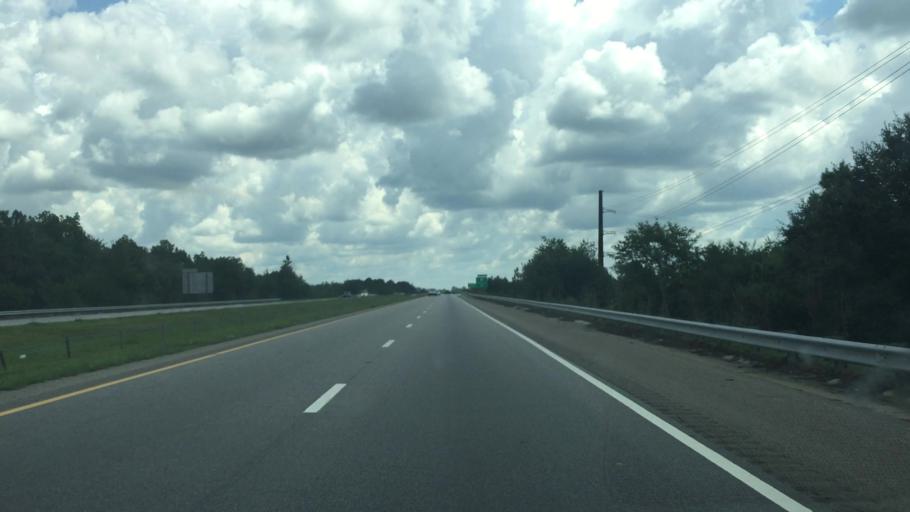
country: US
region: North Carolina
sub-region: Richmond County
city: Hamlet
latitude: 34.8613
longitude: -79.6758
